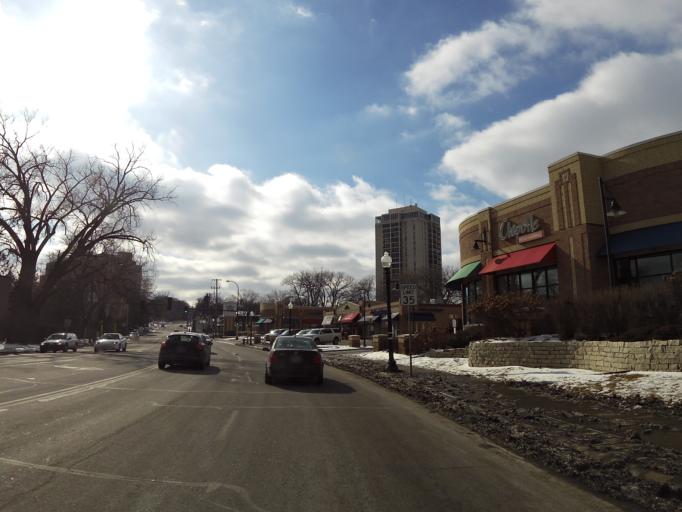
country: US
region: Minnesota
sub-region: Hennepin County
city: Saint Louis Park
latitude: 44.9475
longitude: -93.3209
